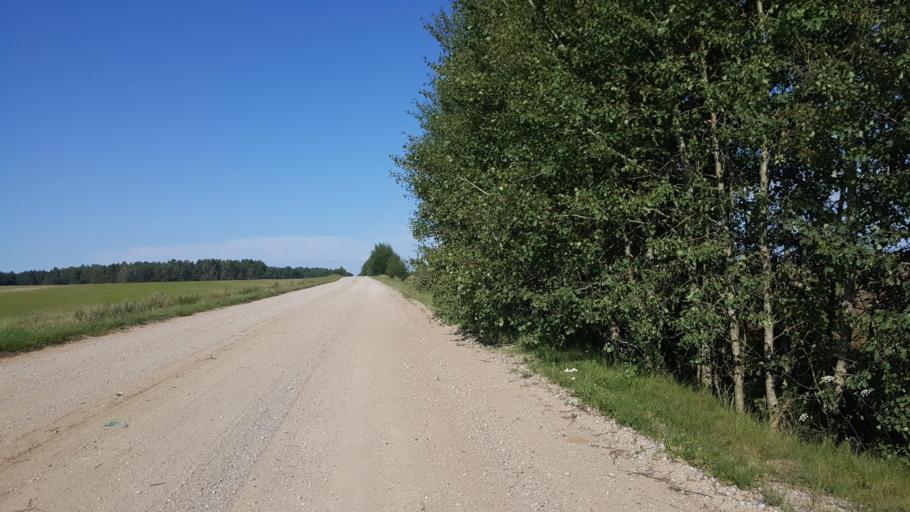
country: BY
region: Brest
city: Kamyanyets
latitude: 52.3595
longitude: 23.7027
